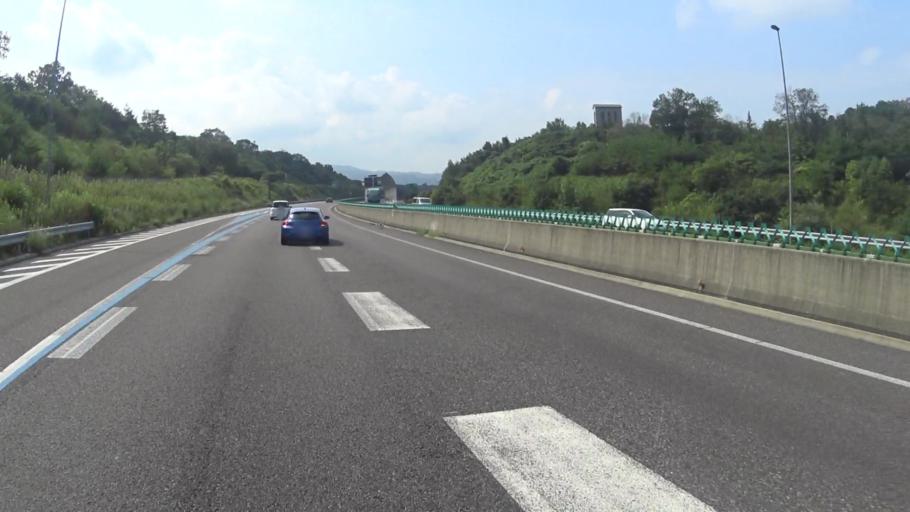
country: JP
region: Shiga Prefecture
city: Kusatsu
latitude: 34.9790
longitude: 135.9610
